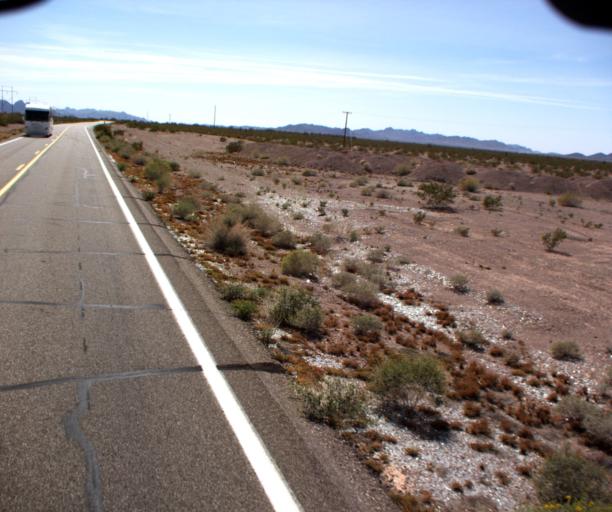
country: US
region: Arizona
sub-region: La Paz County
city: Quartzsite
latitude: 33.4145
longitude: -114.2170
